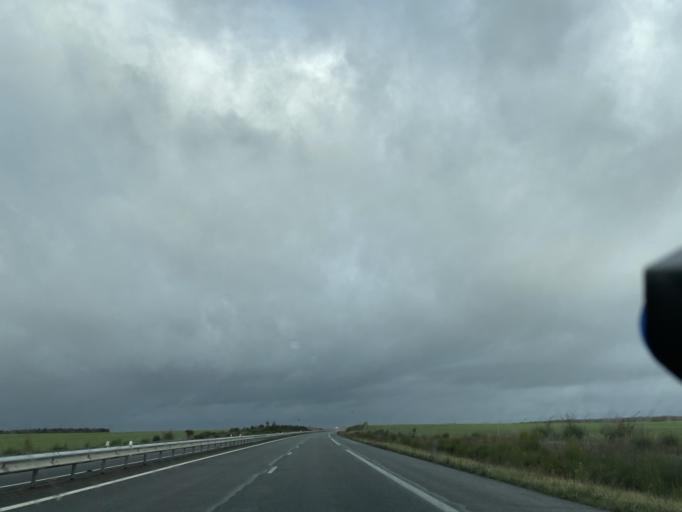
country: FR
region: Centre
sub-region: Departement du Cher
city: Levet
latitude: 46.8261
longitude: 2.4127
